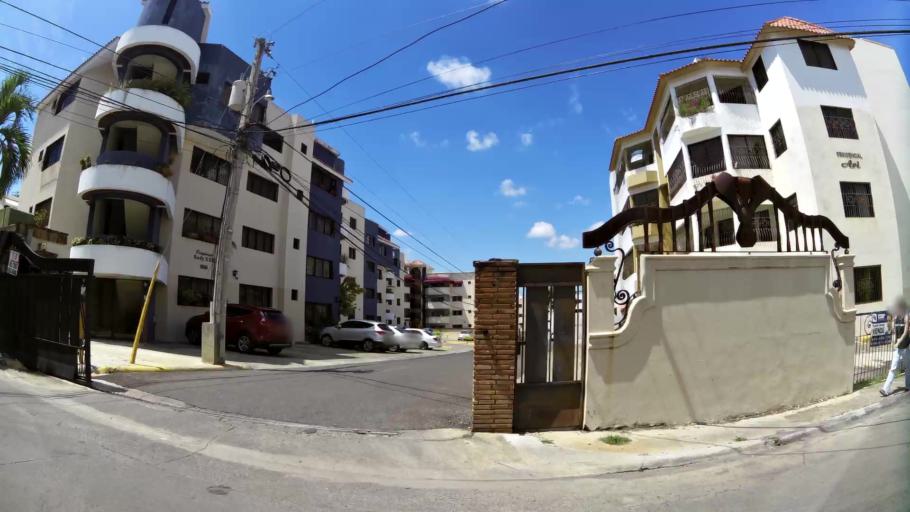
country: DO
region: Santiago
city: Santiago de los Caballeros
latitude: 19.4727
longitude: -70.6769
